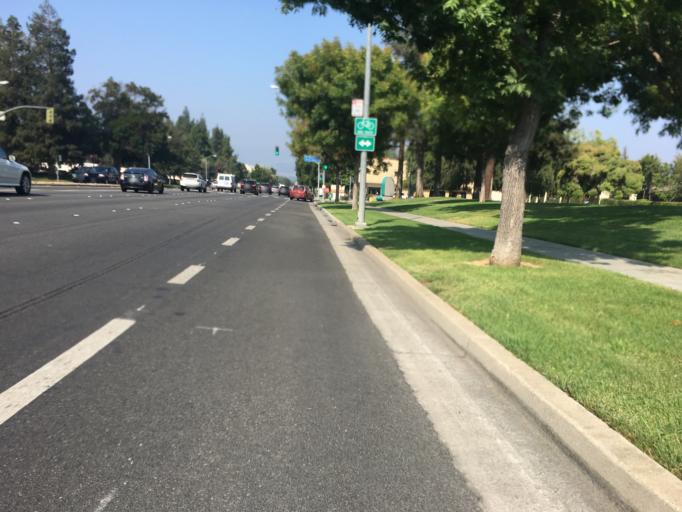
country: US
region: California
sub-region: Santa Clara County
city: Cupertino
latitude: 37.3231
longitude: -122.0188
